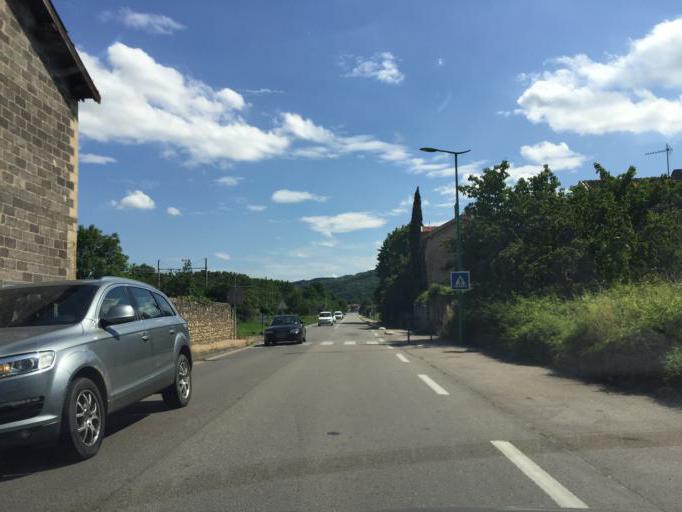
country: FR
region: Rhone-Alpes
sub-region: Departement de l'Ardeche
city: Sarras
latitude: 45.1979
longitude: 4.8013
